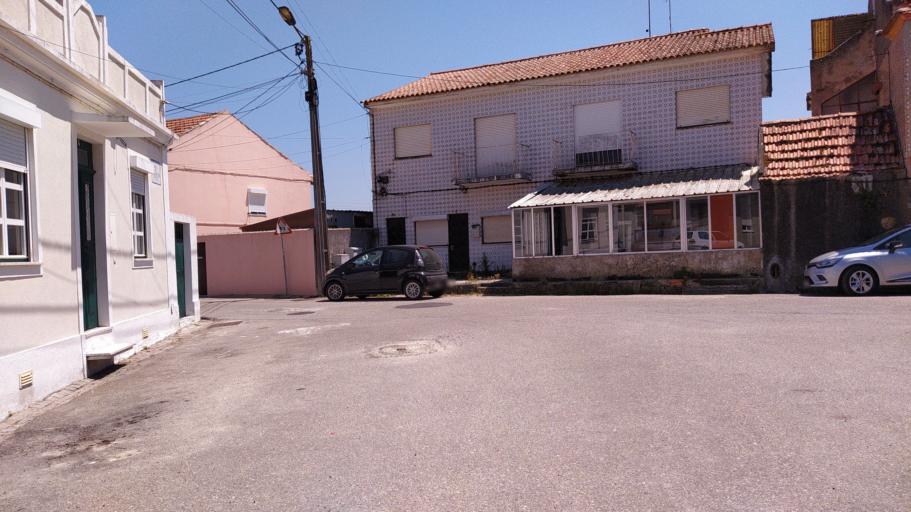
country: PT
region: Aveiro
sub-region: Aveiro
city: Aveiro
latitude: 40.6452
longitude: -8.6362
